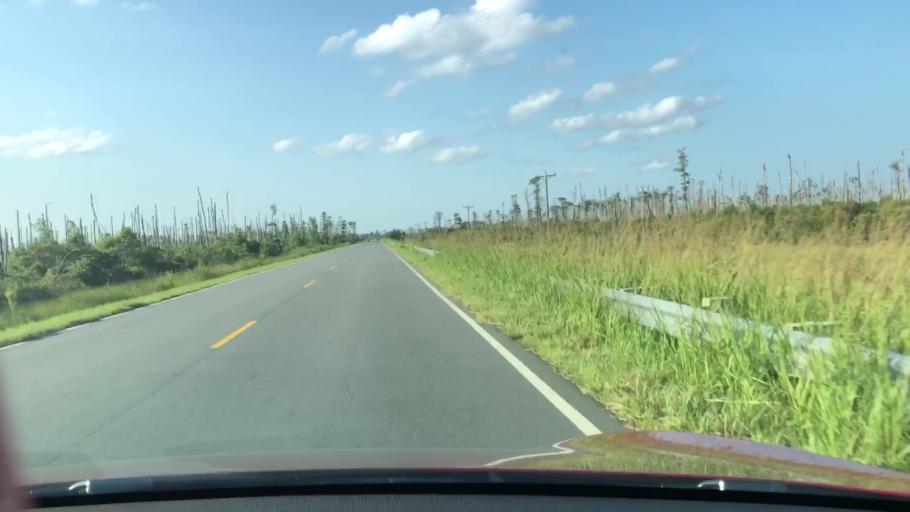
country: US
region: North Carolina
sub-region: Dare County
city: Wanchese
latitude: 35.6512
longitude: -75.7771
